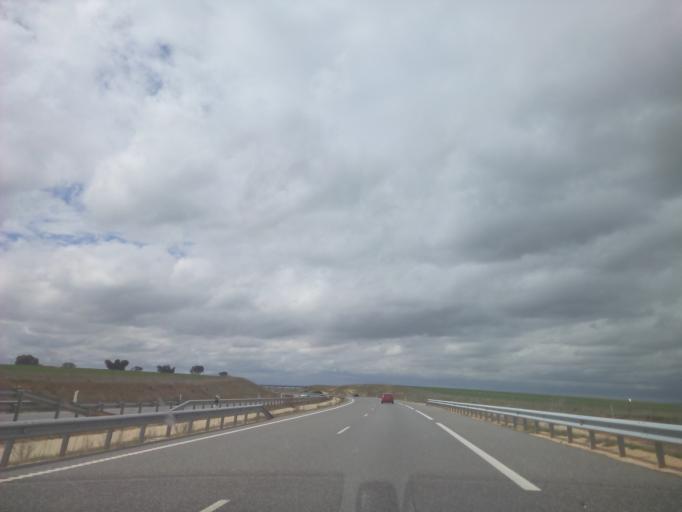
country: ES
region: Castille and Leon
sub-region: Provincia de Salamanca
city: Machacon
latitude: 40.9276
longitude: -5.5402
